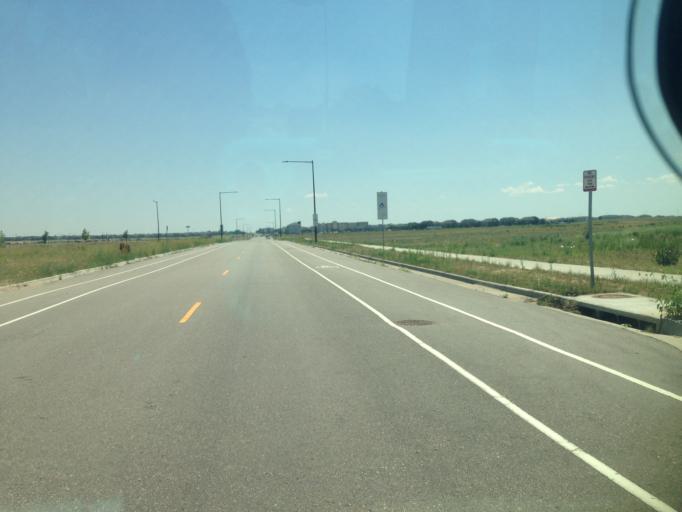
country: US
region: Colorado
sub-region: Adams County
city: Aurora
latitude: 39.8055
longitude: -104.7815
